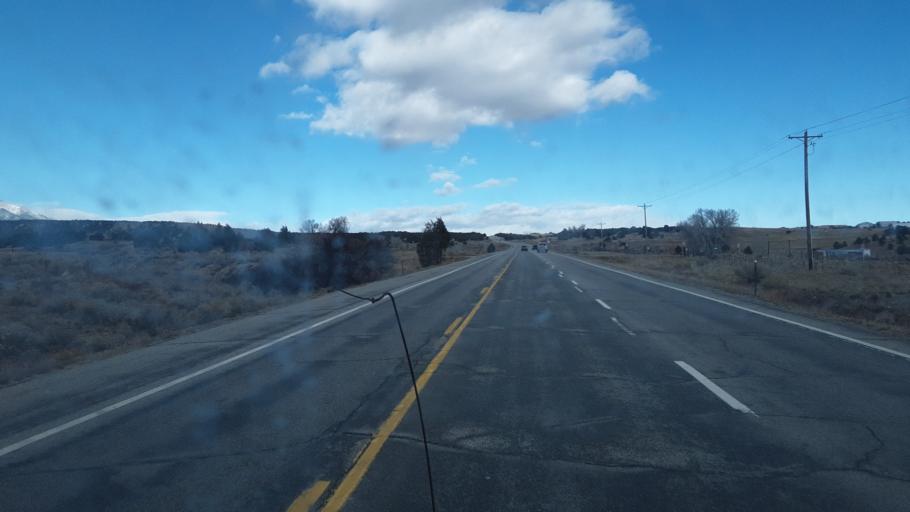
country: US
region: Colorado
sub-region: Chaffee County
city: Salida
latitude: 38.6465
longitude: -106.0839
